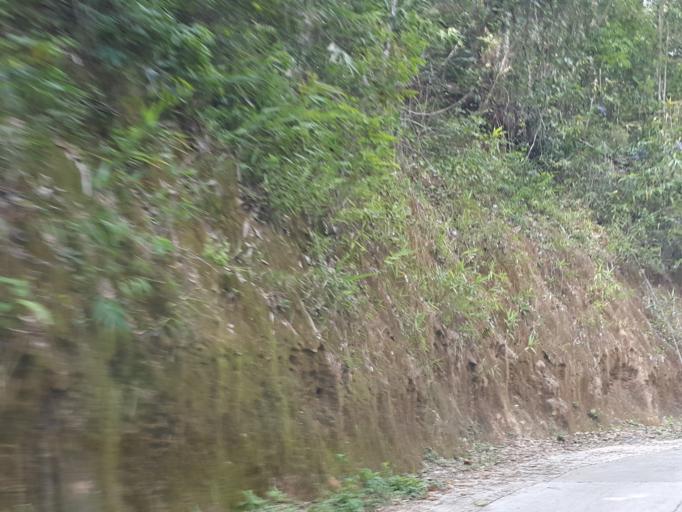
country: TH
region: Chiang Mai
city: Mae On
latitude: 18.8866
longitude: 99.3586
